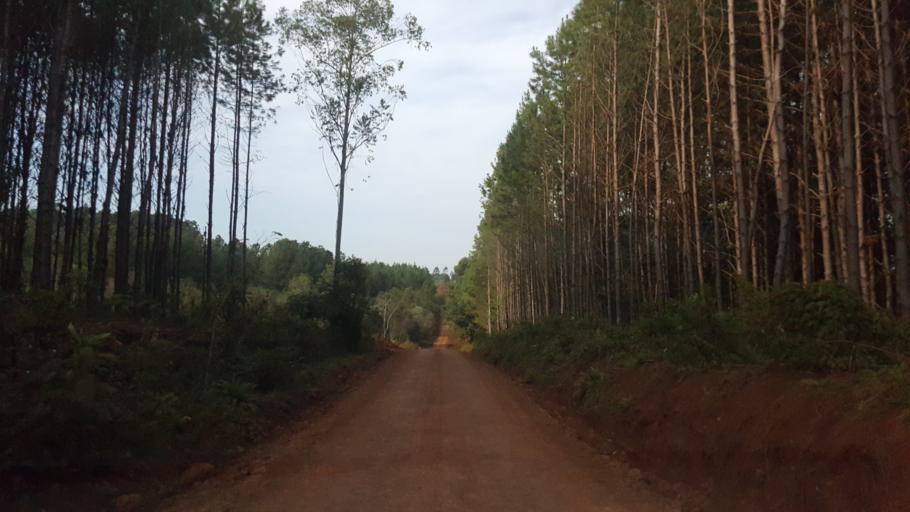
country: AR
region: Misiones
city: Capiovi
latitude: -26.9152
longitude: -55.1166
